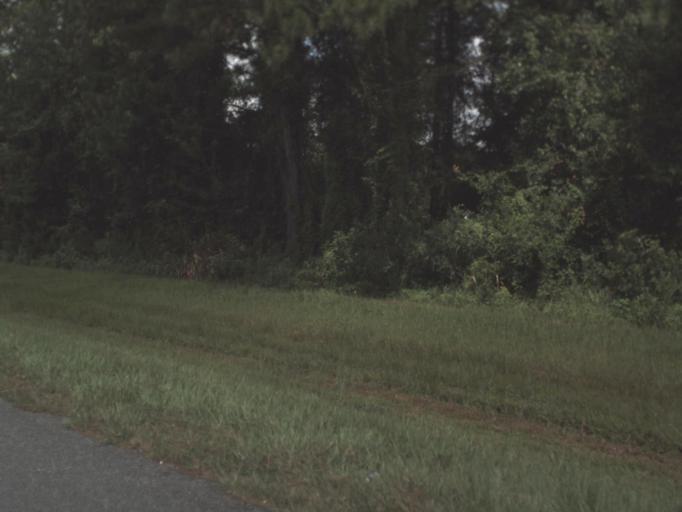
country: US
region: Florida
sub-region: Union County
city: Lake Butler
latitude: 30.0457
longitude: -82.2739
